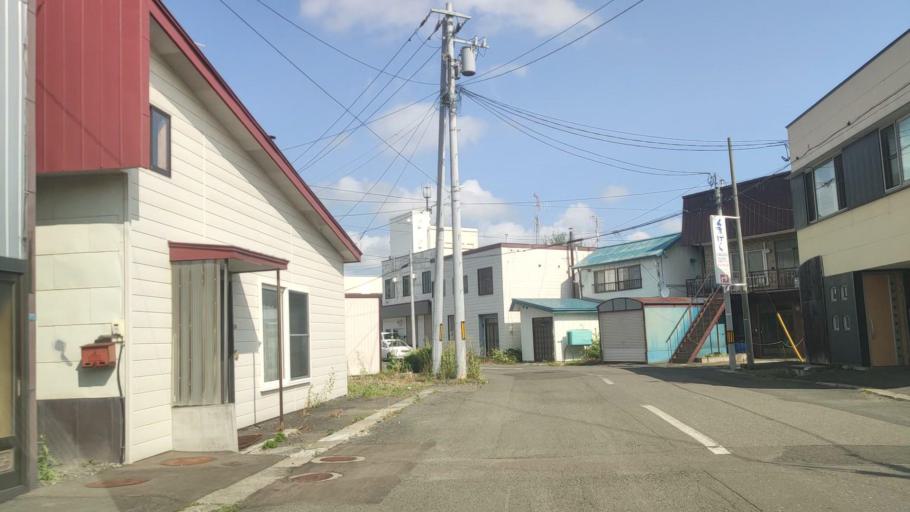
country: JP
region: Hokkaido
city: Shimo-furano
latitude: 43.3444
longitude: 142.3912
